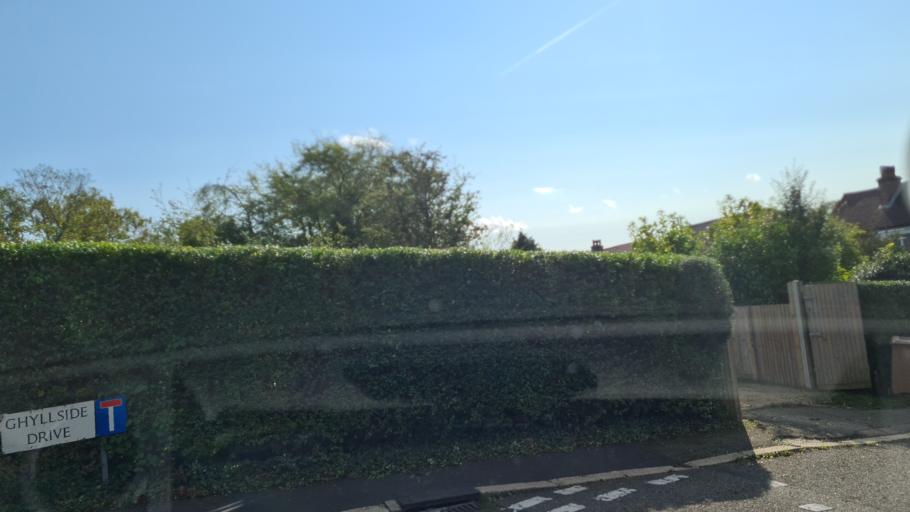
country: GB
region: England
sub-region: East Sussex
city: Hastings
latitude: 50.8752
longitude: 0.5643
